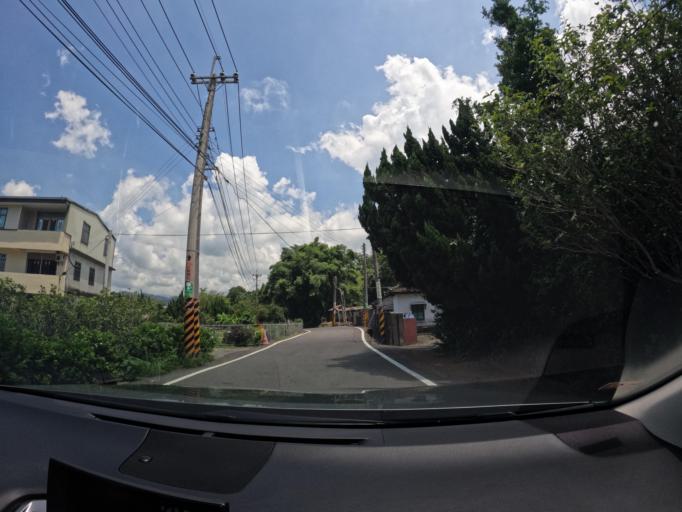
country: TW
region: Taiwan
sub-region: Miaoli
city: Miaoli
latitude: 24.4086
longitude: 120.7854
